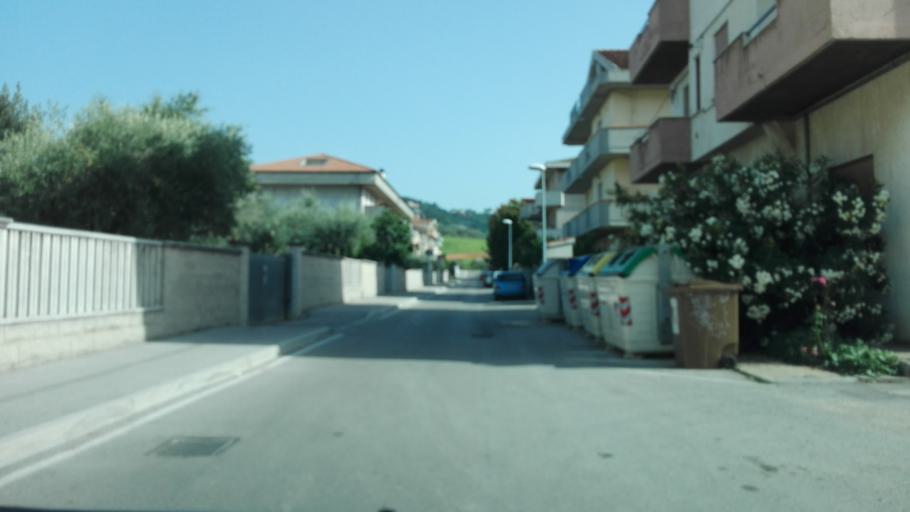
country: IT
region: Abruzzo
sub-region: Provincia di Pescara
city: Montesilvano Marina
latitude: 42.5111
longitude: 14.1479
